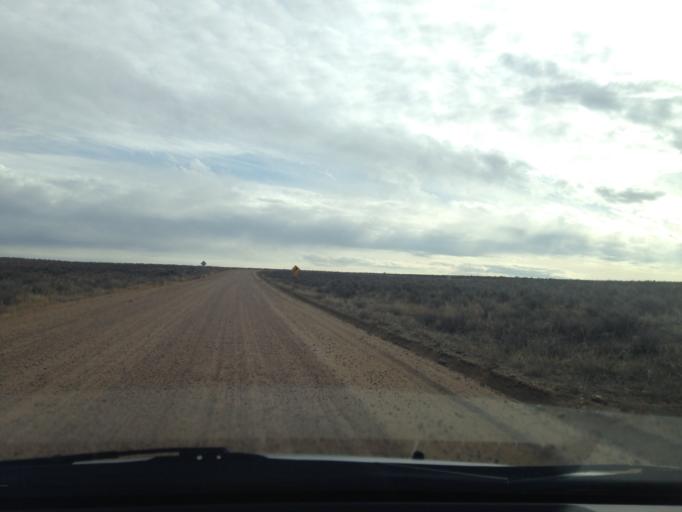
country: US
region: Colorado
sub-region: Weld County
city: Keenesburg
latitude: 40.2754
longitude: -104.2070
